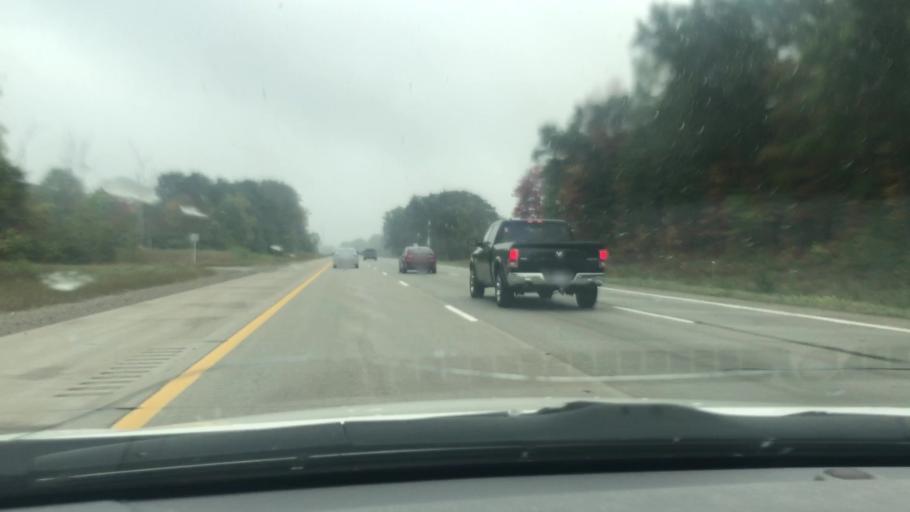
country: US
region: Michigan
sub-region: Livingston County
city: Brighton
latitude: 42.5731
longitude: -83.8493
